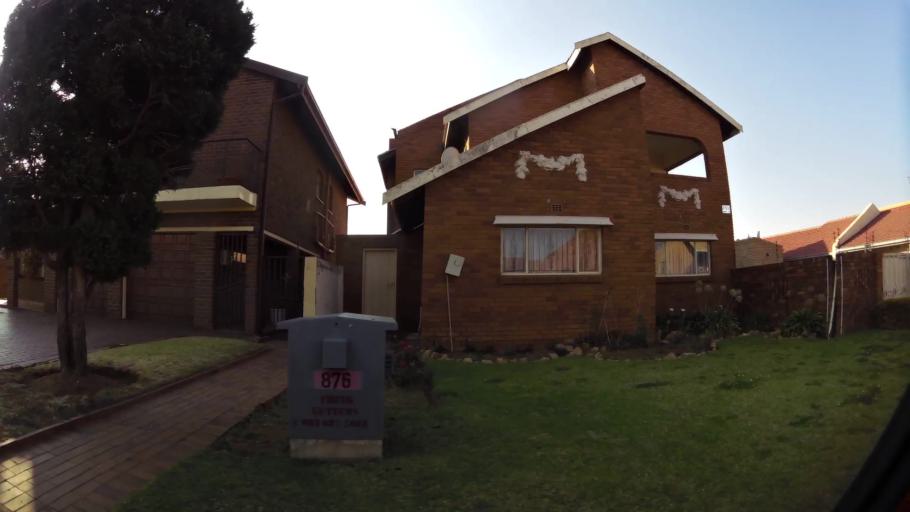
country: ZA
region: Gauteng
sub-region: City of Johannesburg Metropolitan Municipality
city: Johannesburg
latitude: -26.2516
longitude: 27.9615
